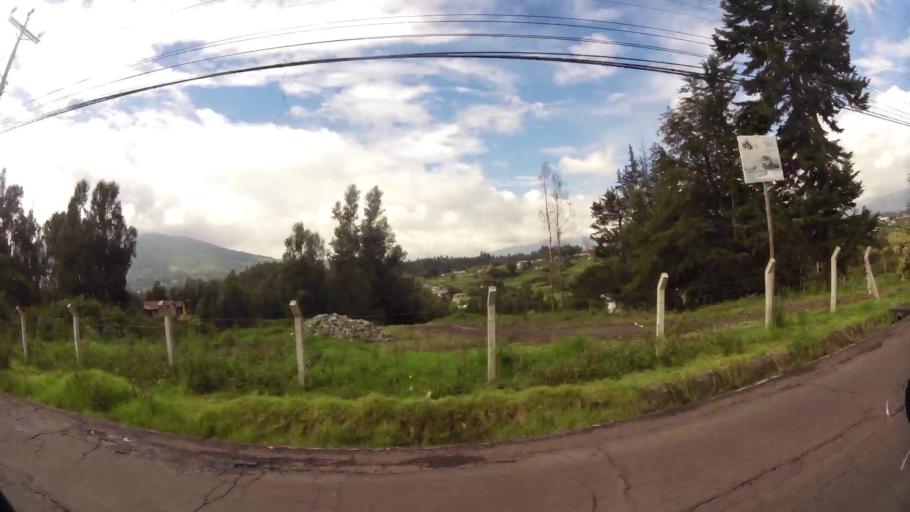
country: EC
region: Pichincha
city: Sangolqui
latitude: -0.3114
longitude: -78.4094
